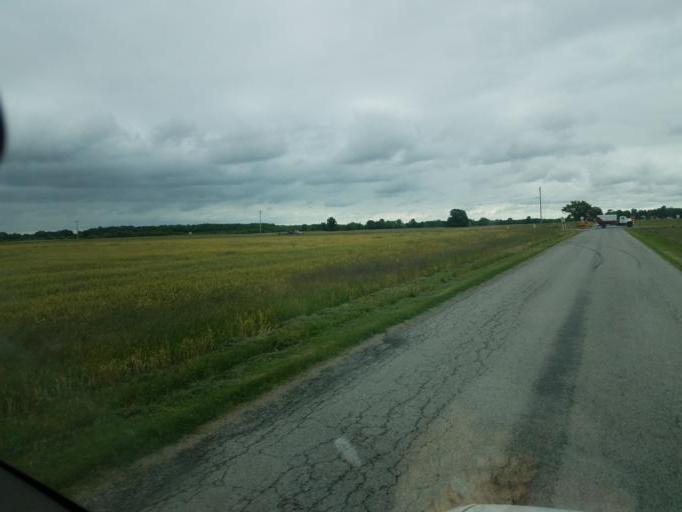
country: US
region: Ohio
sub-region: Morrow County
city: Cardington
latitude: 40.5588
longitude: -82.9194
